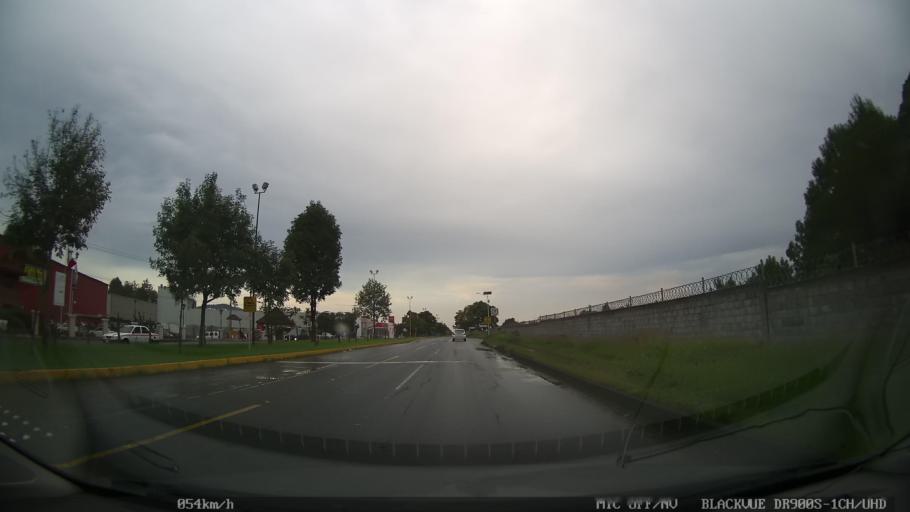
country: MX
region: Michoacan
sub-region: Uruapan
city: Santa Rosa (Santa Barbara)
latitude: 19.3898
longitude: -102.0402
